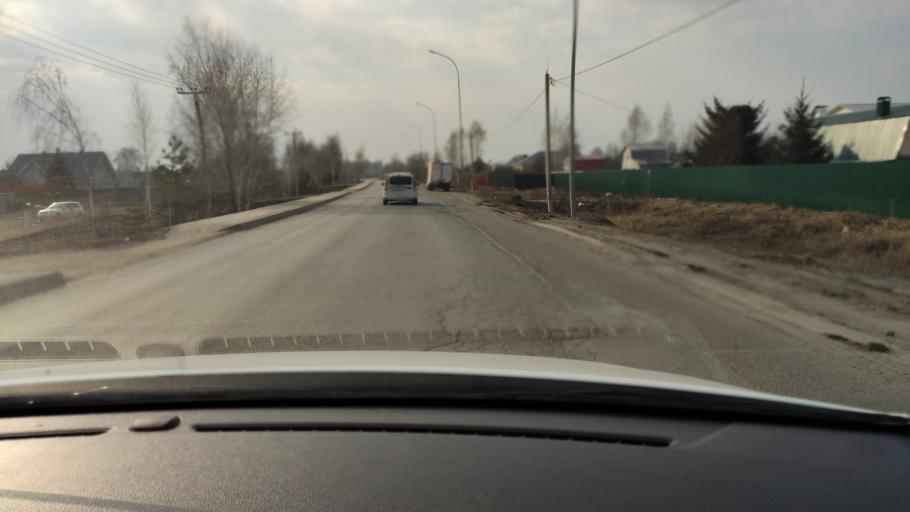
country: RU
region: Tatarstan
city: Stolbishchi
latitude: 55.6940
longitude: 49.2091
